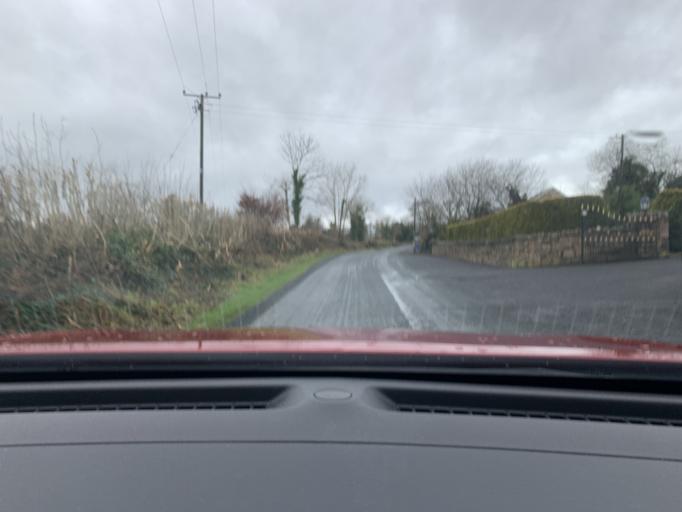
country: IE
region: Connaught
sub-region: Sligo
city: Collooney
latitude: 54.2026
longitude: -8.4278
